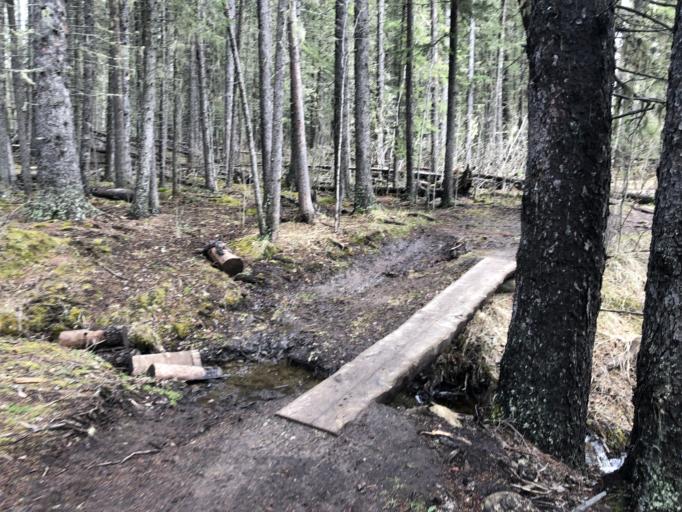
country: CA
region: Alberta
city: Cochrane
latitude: 51.0398
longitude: -114.7430
